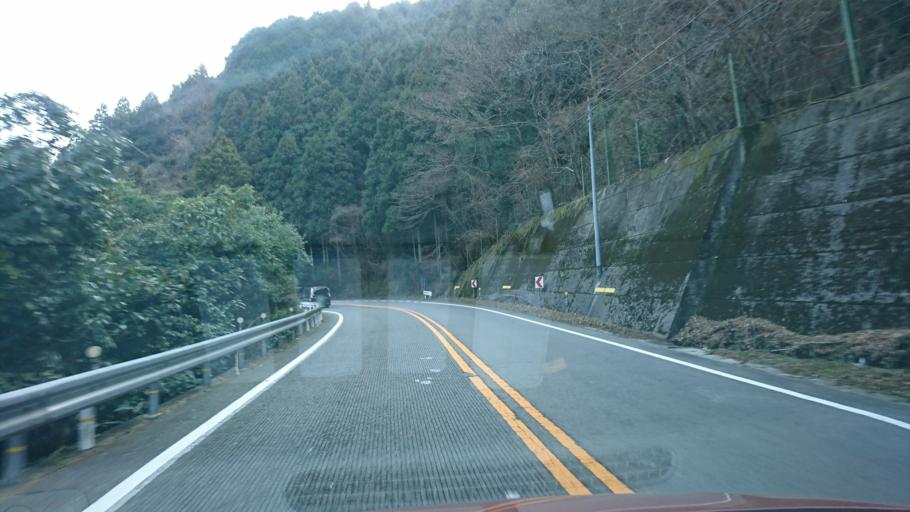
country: JP
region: Ehime
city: Hojo
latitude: 33.9650
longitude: 132.9058
